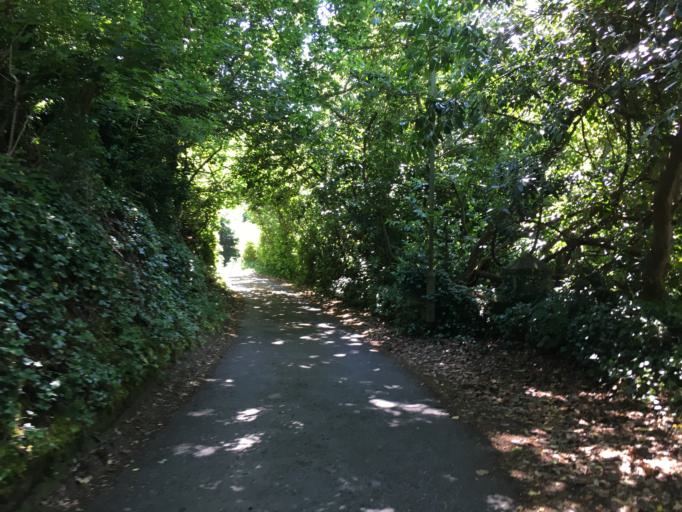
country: GB
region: England
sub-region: Devon
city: Dartmouth
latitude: 50.3447
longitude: -3.5627
